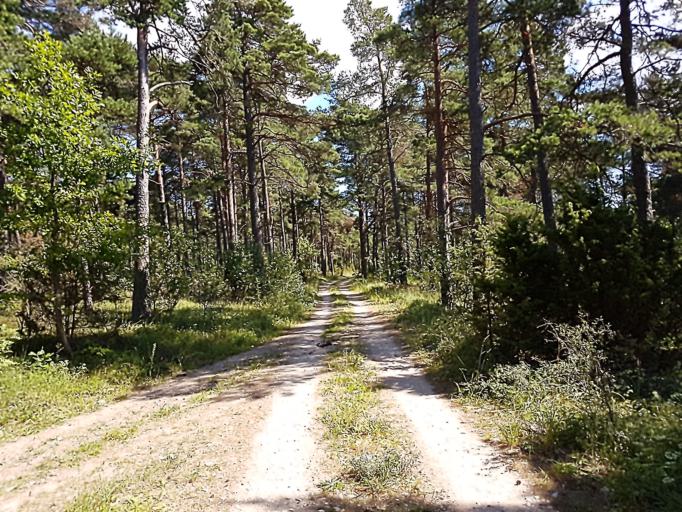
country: SE
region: Gotland
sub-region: Gotland
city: Visby
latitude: 57.6074
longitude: 18.3377
